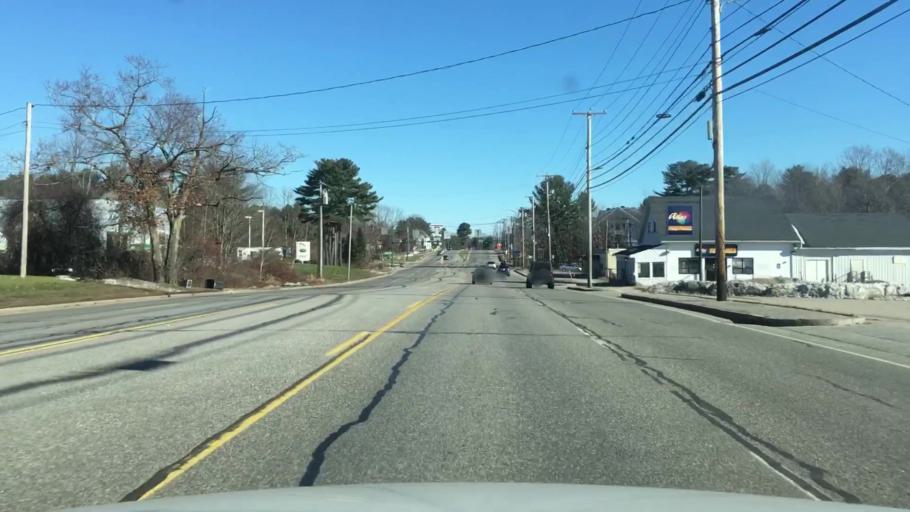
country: US
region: Maine
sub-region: Cumberland County
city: West Scarborough
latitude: 43.5852
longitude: -70.3573
